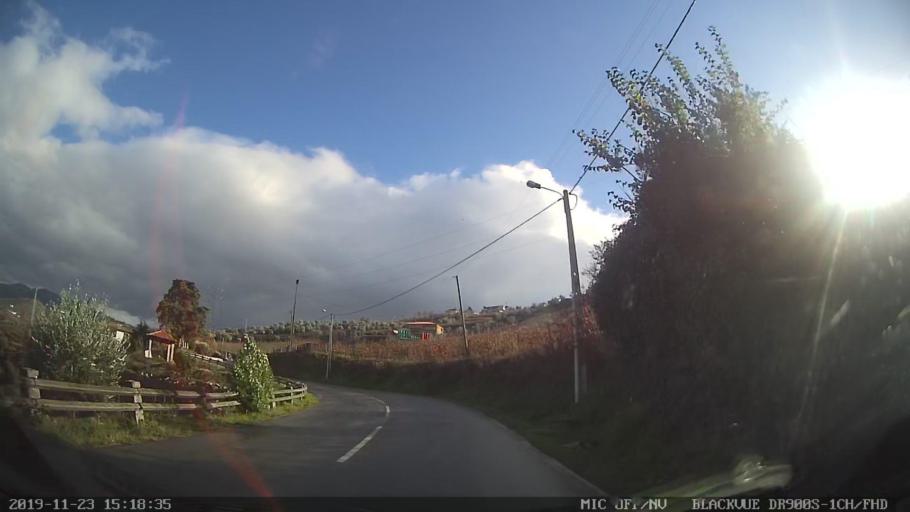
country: PT
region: Viseu
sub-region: Lamego
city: Lamego
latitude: 41.1187
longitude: -7.7953
